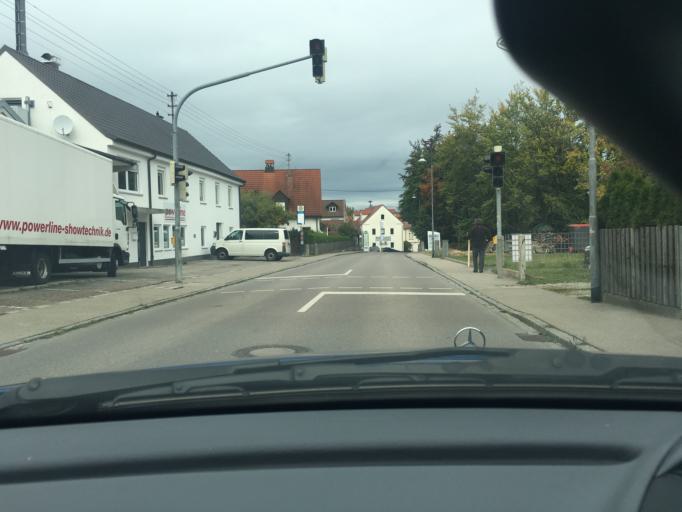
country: DE
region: Bavaria
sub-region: Swabia
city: Gablingen
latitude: 48.4098
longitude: 10.8240
